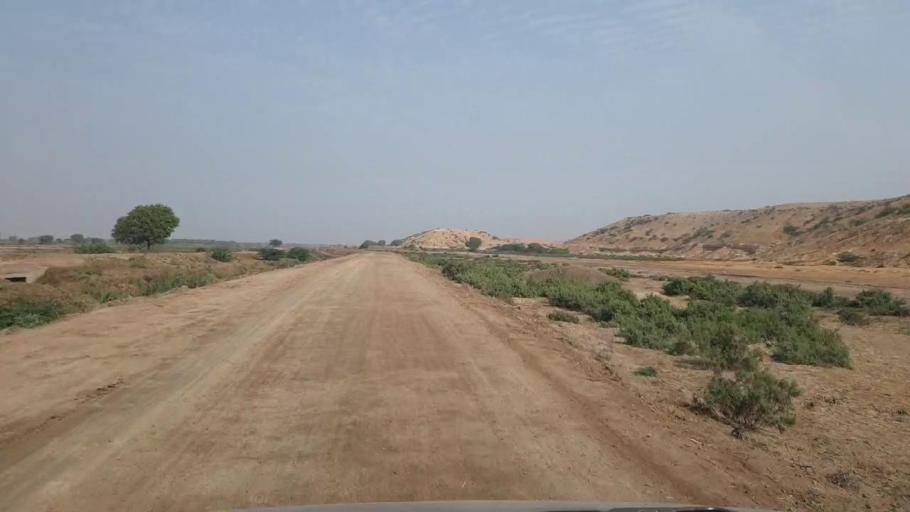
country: PK
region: Sindh
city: Tando Muhammad Khan
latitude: 25.1405
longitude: 68.4565
